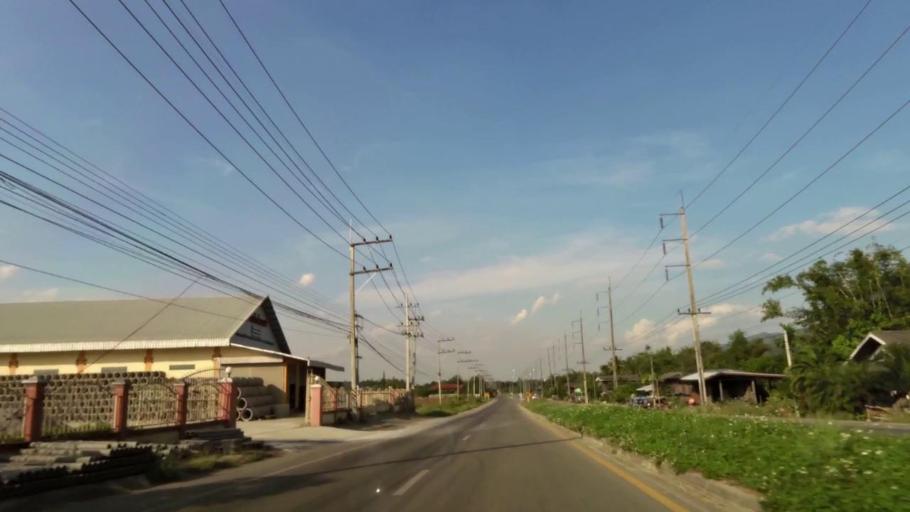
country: TH
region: Chiang Rai
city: Khun Tan
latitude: 19.9006
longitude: 100.2957
